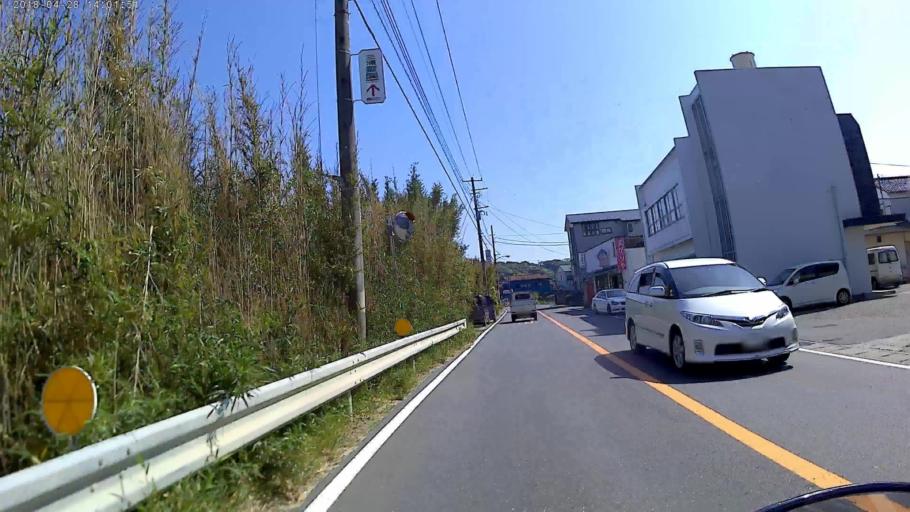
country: JP
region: Kanagawa
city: Miura
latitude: 35.1654
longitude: 139.6596
